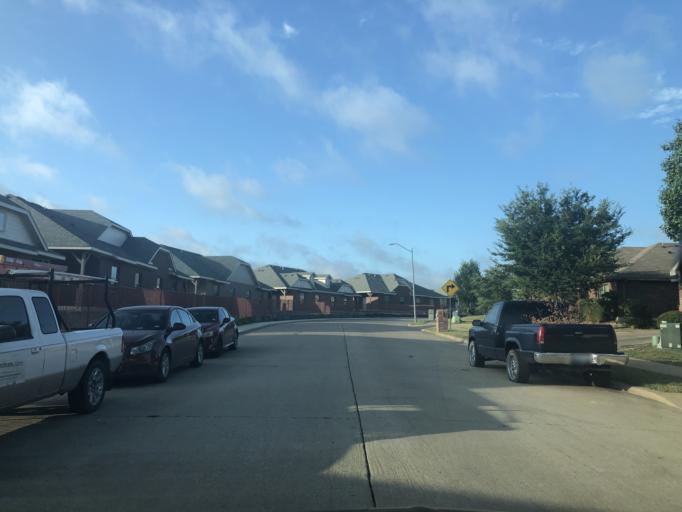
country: US
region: Texas
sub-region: Dallas County
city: Duncanville
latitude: 32.6650
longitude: -96.9391
